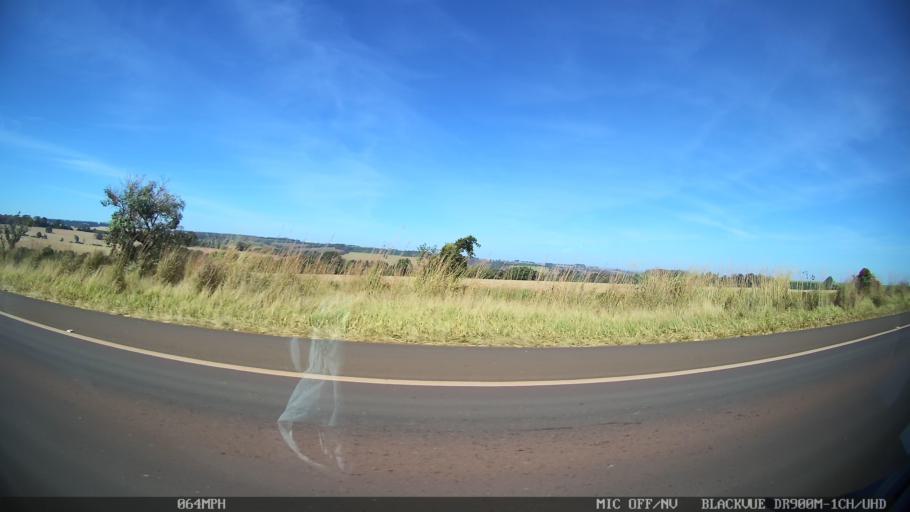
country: BR
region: Sao Paulo
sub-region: Franca
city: Franca
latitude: -20.5531
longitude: -47.4908
